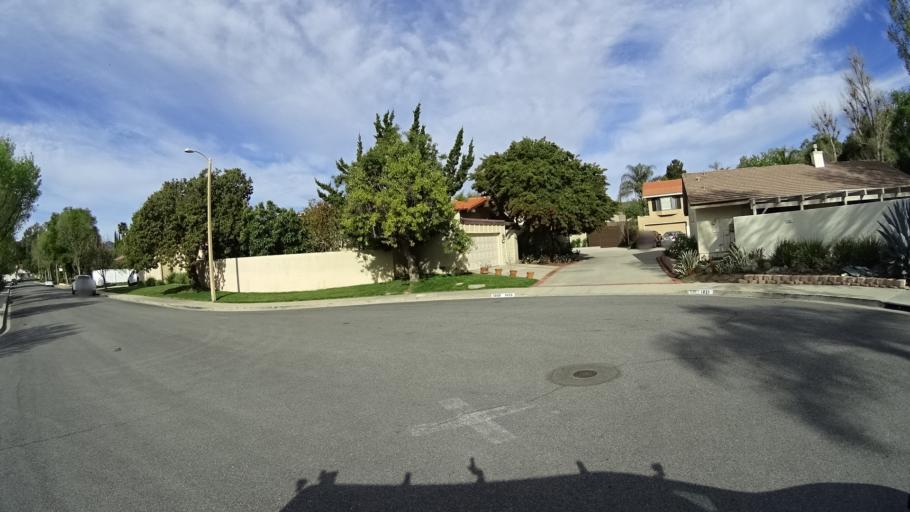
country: US
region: California
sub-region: Ventura County
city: Thousand Oaks
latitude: 34.1515
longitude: -118.8373
